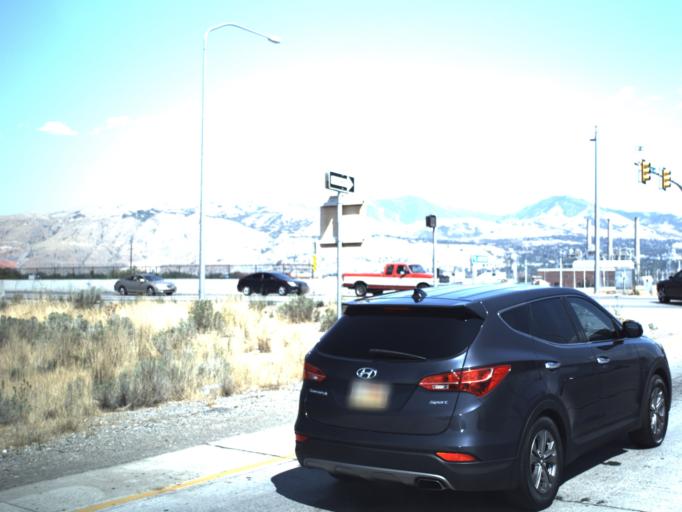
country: US
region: Utah
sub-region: Salt Lake County
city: Salt Lake City
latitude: 40.7654
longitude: -111.9397
